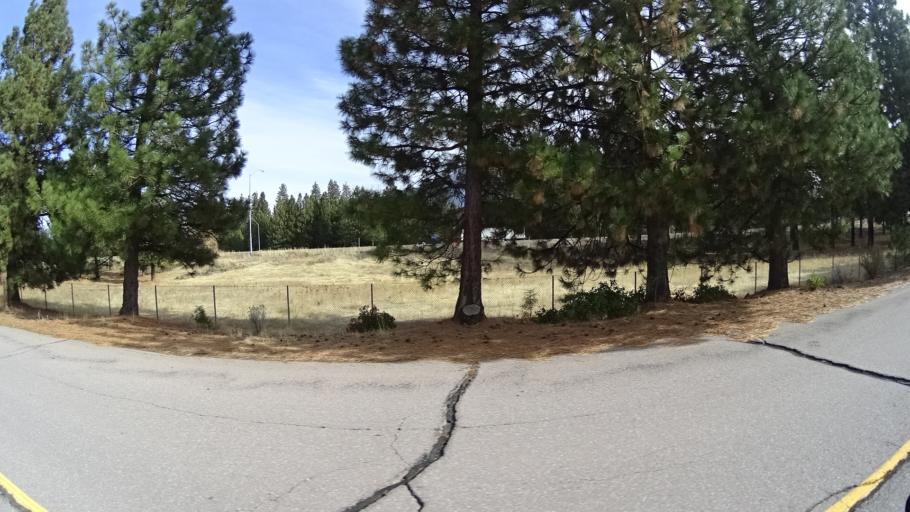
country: US
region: California
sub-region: Siskiyou County
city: Weed
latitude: 41.3999
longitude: -122.3838
